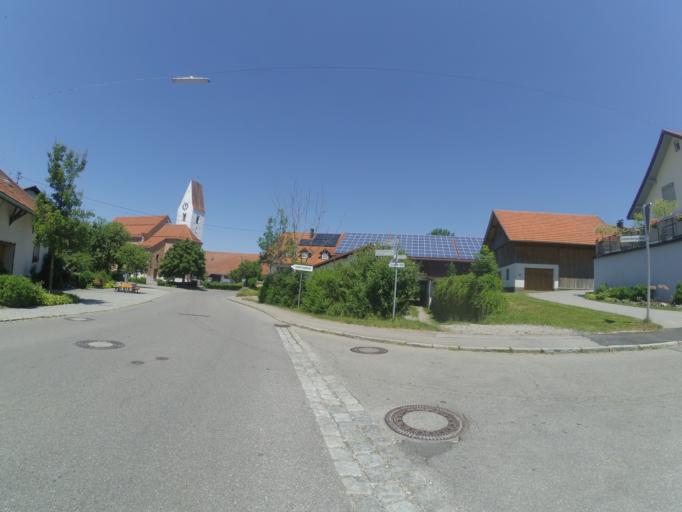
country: DE
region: Bavaria
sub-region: Swabia
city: Untrasried
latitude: 47.8535
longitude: 10.3551
